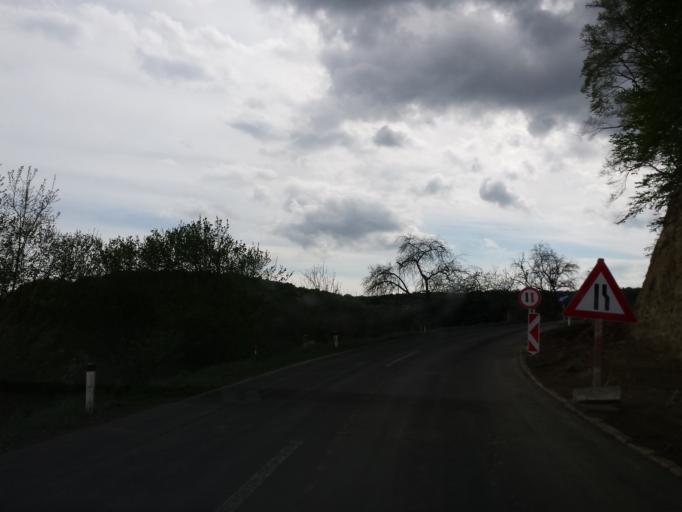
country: AT
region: Styria
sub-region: Politischer Bezirk Hartberg-Fuerstenfeld
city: UEbersbach
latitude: 47.0143
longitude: 16.0462
